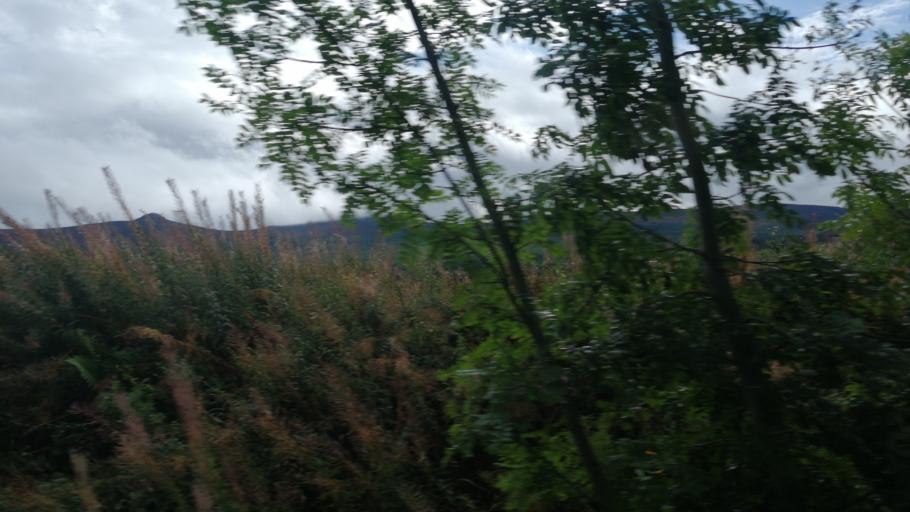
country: GB
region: Scotland
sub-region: Aberdeenshire
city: Insch
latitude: 57.3232
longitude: -2.5570
